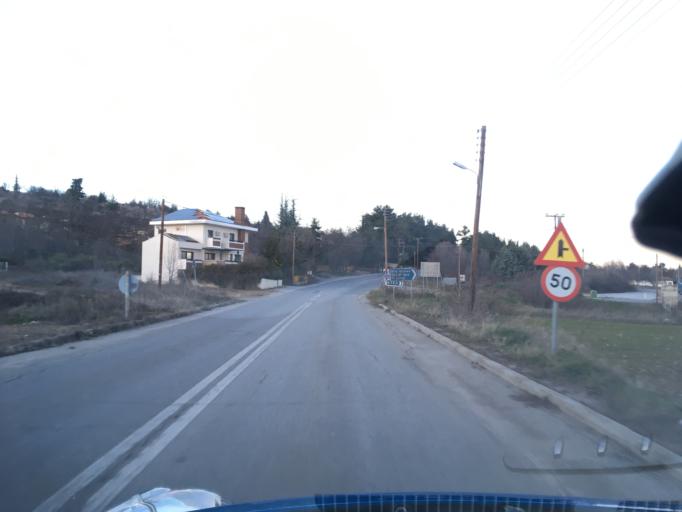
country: GR
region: West Macedonia
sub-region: Nomos Kozanis
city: Kozani
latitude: 40.2734
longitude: 21.7816
